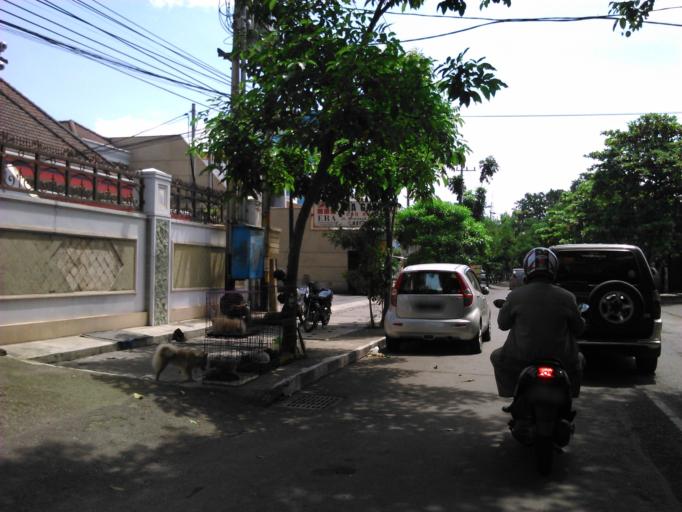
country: ID
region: East Java
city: Gubengairlangga
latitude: -7.2803
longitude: 112.7420
